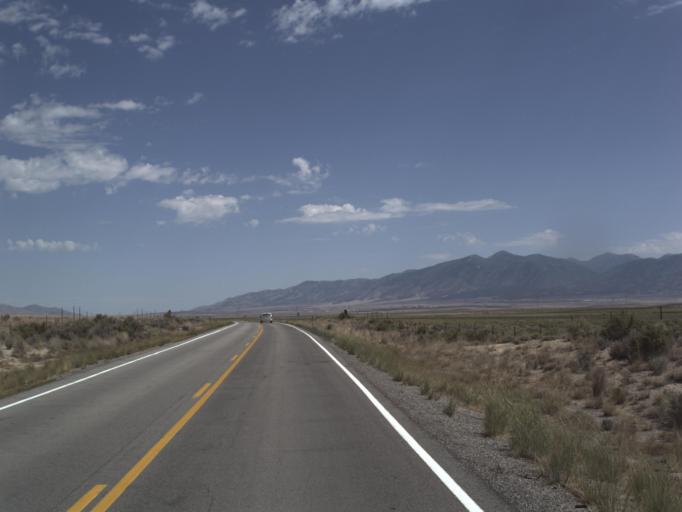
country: US
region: Utah
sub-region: Tooele County
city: Tooele
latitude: 40.2080
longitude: -112.4088
